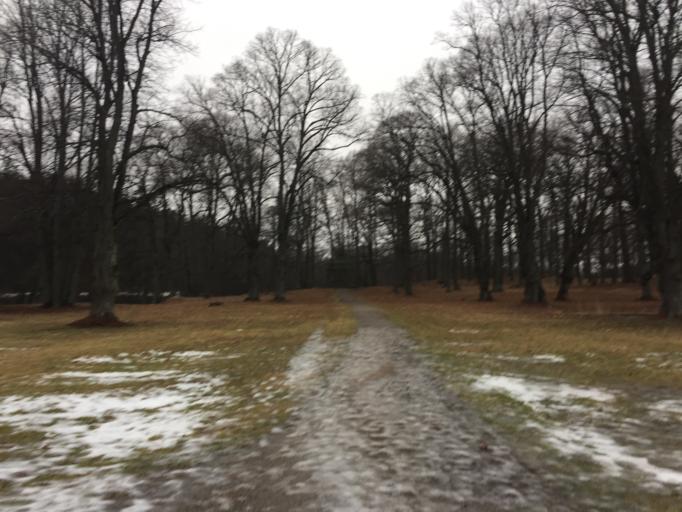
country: SE
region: Stockholm
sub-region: Norrtalje Kommun
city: Bergshamra
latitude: 59.3897
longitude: 18.0116
